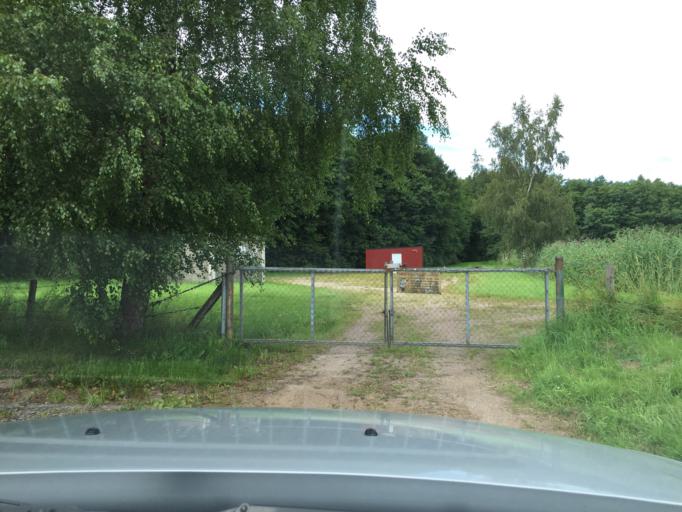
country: SE
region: Skane
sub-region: Hassleholms Kommun
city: Sosdala
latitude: 56.0104
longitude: 13.6396
